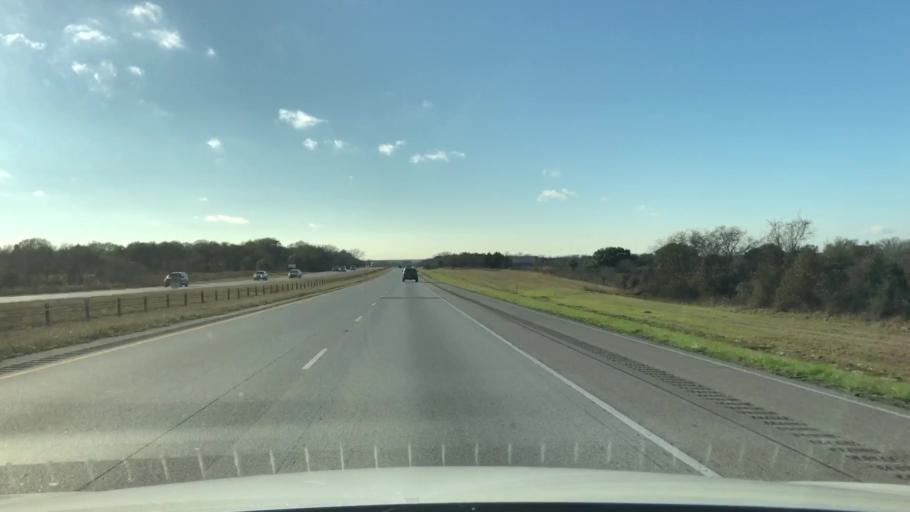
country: US
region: Texas
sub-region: Colorado County
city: Weimar
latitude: 29.6876
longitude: -96.8165
